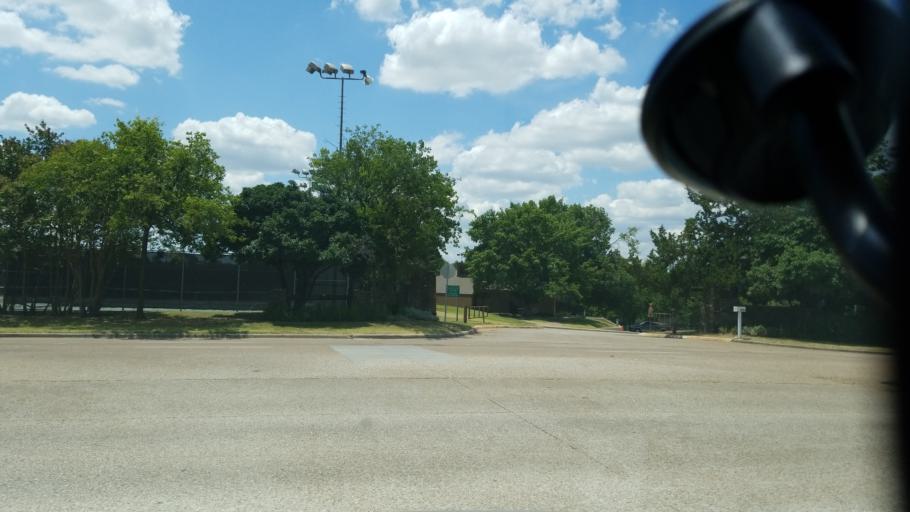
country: US
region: Texas
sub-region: Dallas County
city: Cockrell Hill
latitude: 32.7059
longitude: -96.8544
